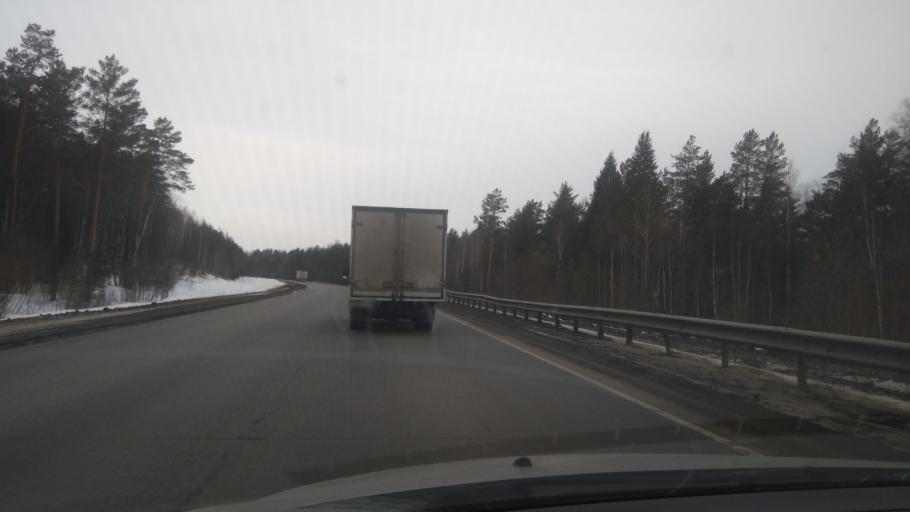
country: RU
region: Sverdlovsk
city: Ufimskiy
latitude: 56.7675
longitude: 58.1761
